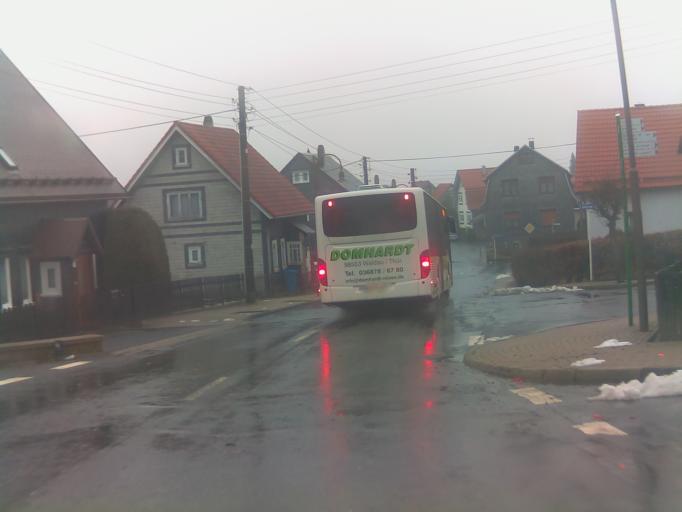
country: DE
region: Thuringia
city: Eisfeld
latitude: 50.4975
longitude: 10.9030
